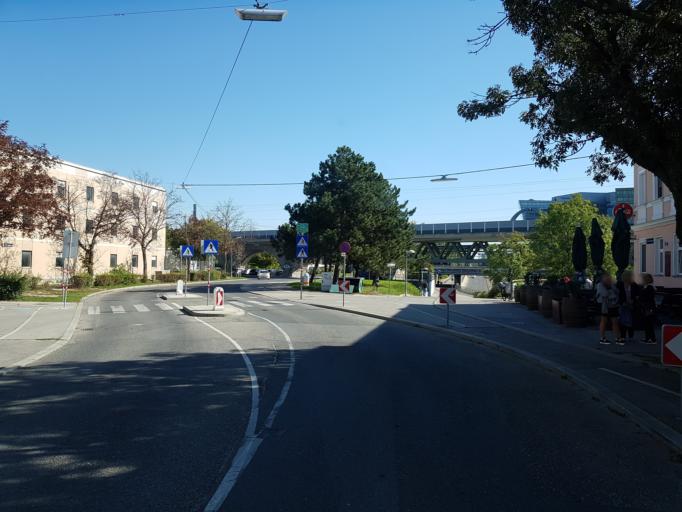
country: AT
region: Lower Austria
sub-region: Politischer Bezirk Wien-Umgebung
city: Gerasdorf bei Wien
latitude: 48.2718
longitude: 16.4192
